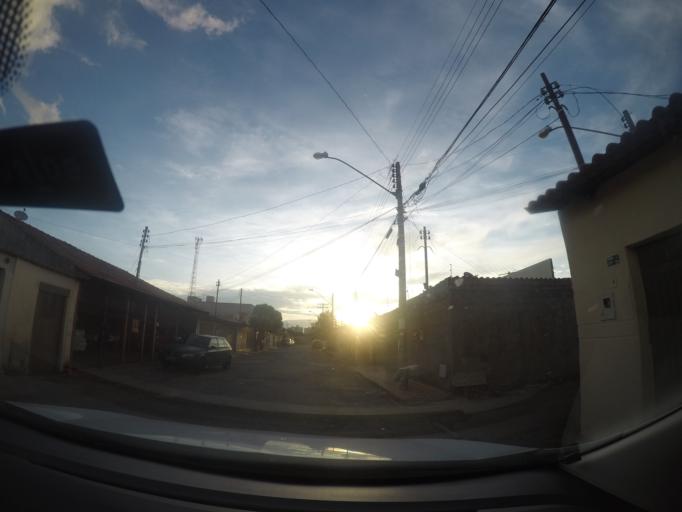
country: BR
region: Goias
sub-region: Goiania
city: Goiania
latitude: -16.6894
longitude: -49.3172
